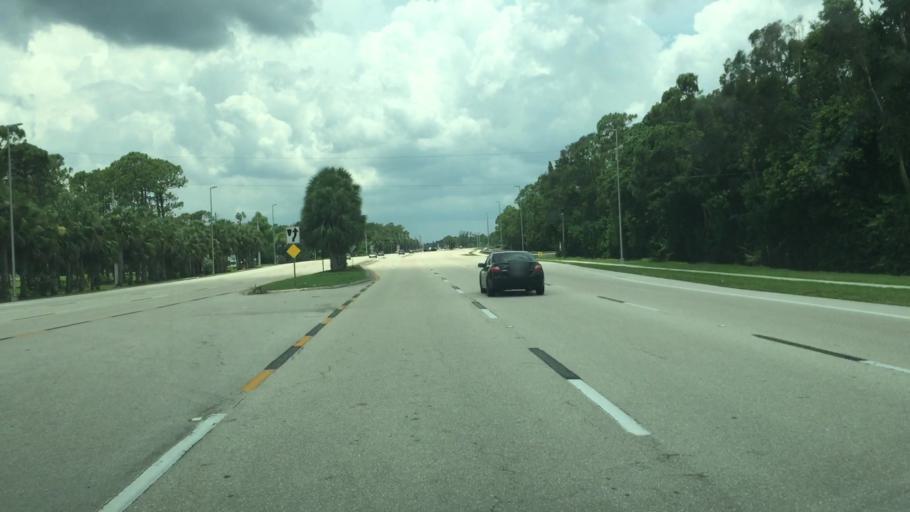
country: US
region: Florida
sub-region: Lee County
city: Villas
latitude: 26.5462
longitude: -81.8565
